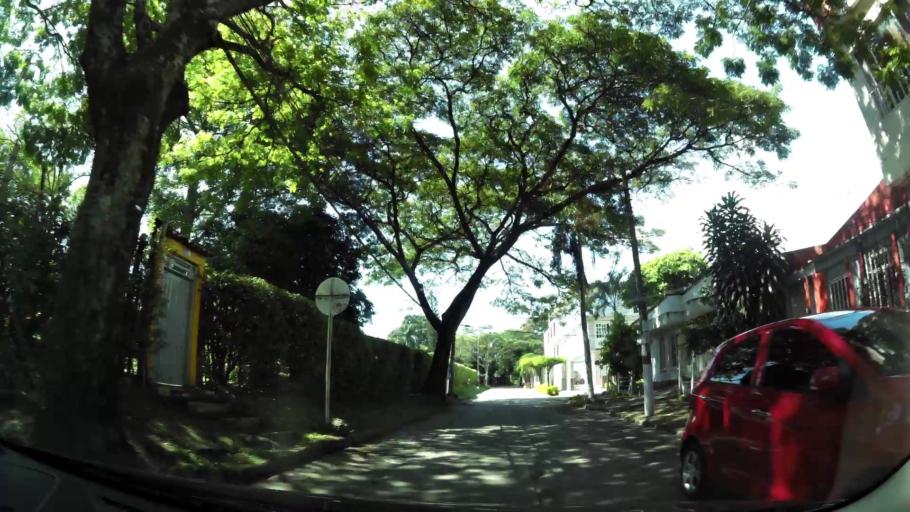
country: CO
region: Valle del Cauca
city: Cali
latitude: 3.4233
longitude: -76.5323
